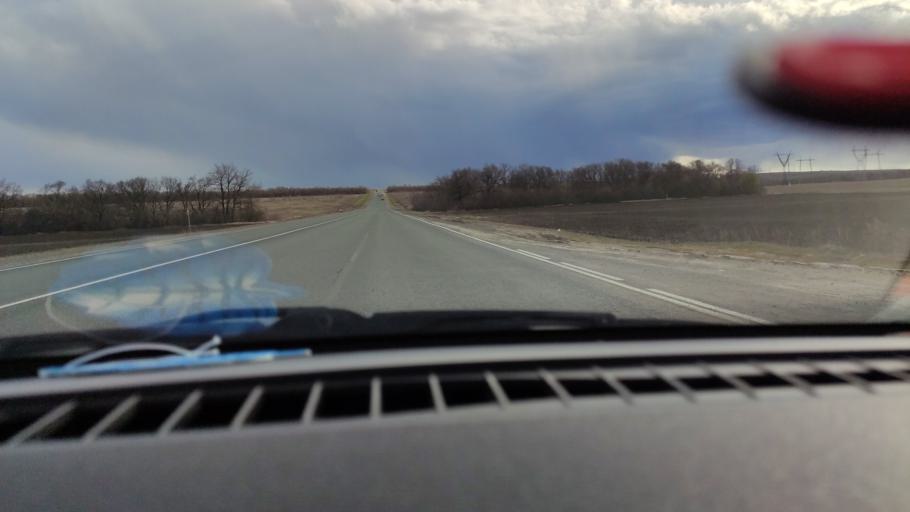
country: RU
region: Saratov
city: Sinodskoye
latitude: 51.9161
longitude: 46.5564
